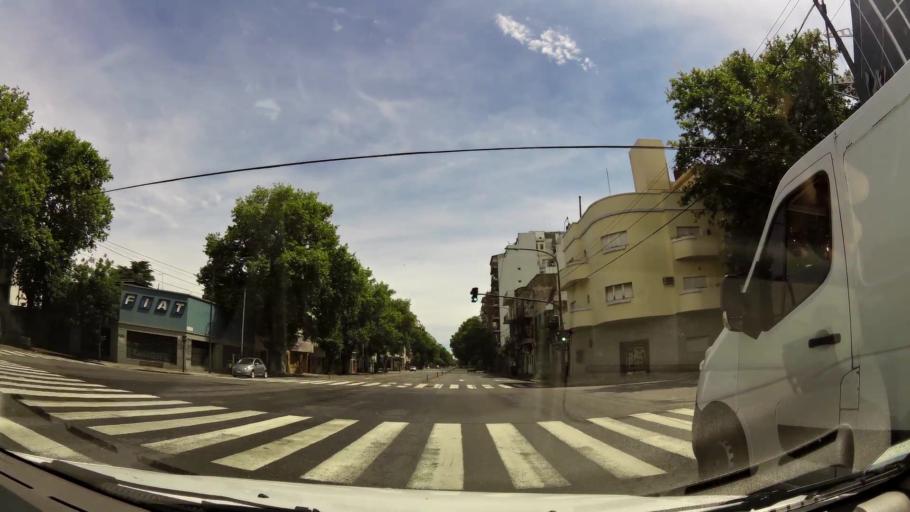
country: AR
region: Buenos Aires F.D.
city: Colegiales
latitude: -34.6007
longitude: -58.4530
